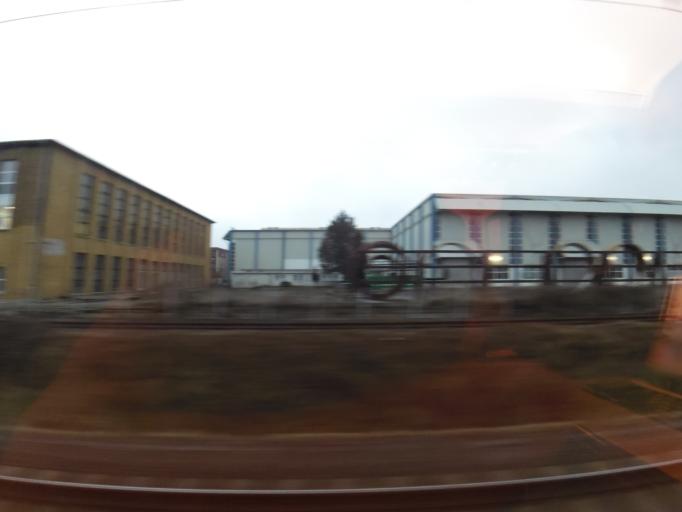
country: DE
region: Saxony
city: Taucha
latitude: 51.3443
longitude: 12.4543
